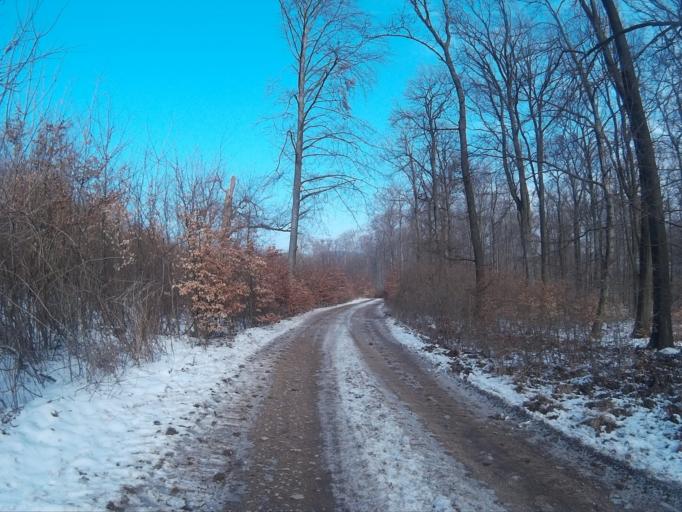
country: HU
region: Komarom-Esztergom
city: Labatlan
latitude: 47.6844
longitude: 18.5084
